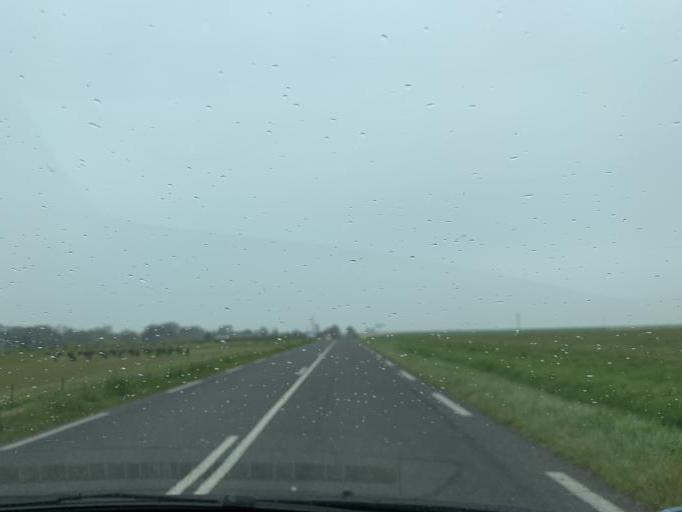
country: FR
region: Haute-Normandie
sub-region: Departement de la Seine-Maritime
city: Cany-Barville
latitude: 49.8027
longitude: 0.6660
